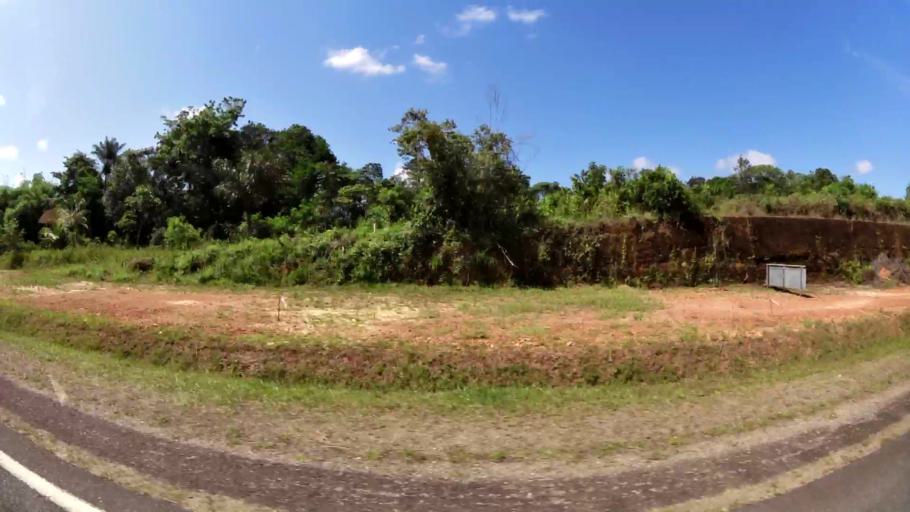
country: GF
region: Guyane
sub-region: Guyane
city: Matoury
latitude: 4.8343
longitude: -52.3259
